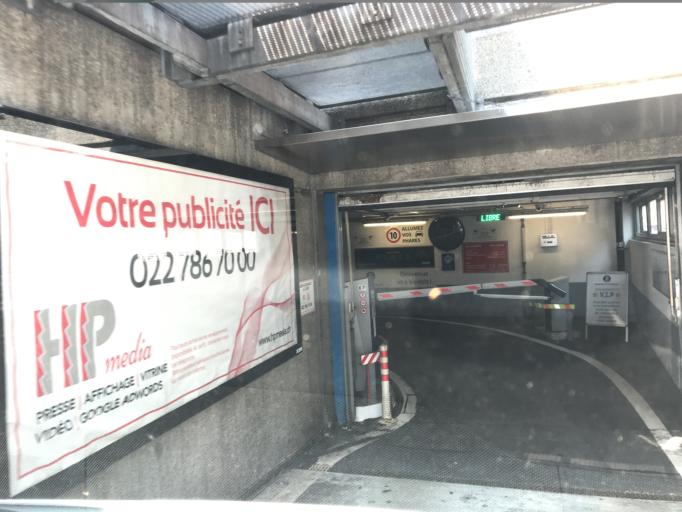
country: CH
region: Vaud
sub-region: Lausanne District
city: Lausanne
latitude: 46.5199
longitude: 6.6309
